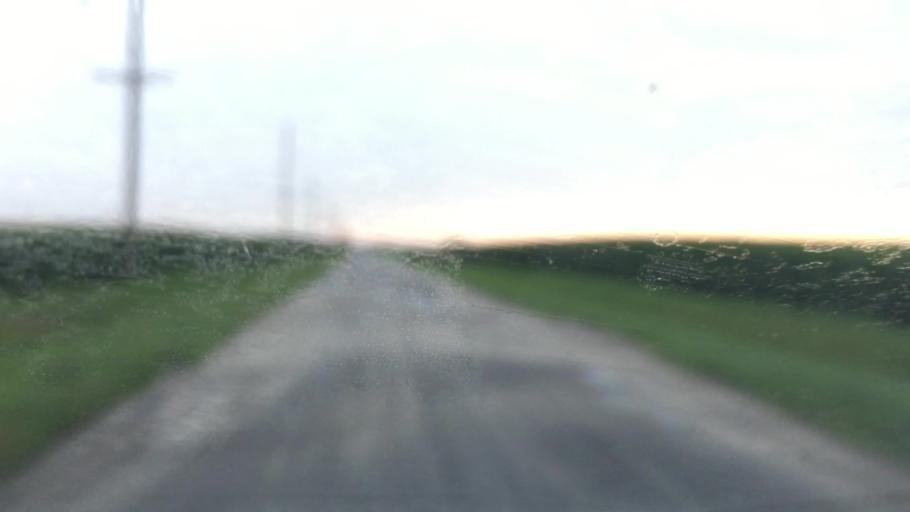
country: US
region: Iowa
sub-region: Lee County
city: Fort Madison
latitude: 40.5522
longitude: -91.2688
